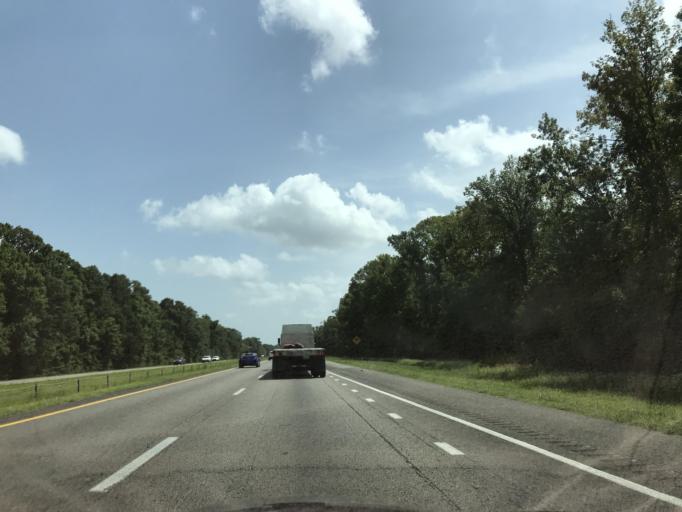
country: US
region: North Carolina
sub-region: Pender County
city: Rocky Point
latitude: 34.4344
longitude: -77.8726
